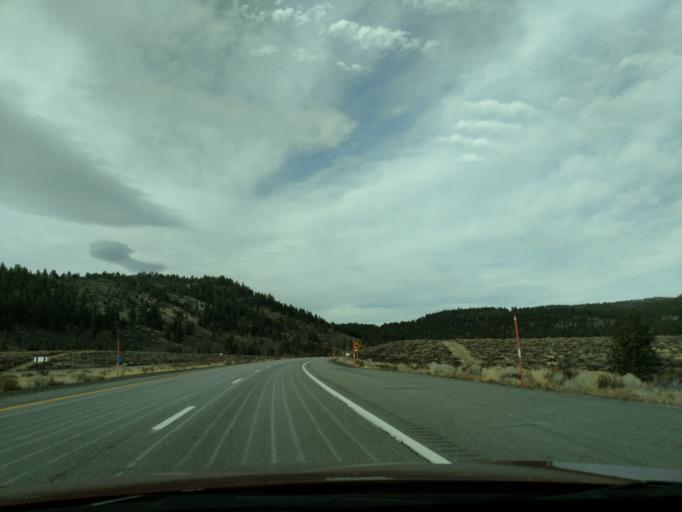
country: US
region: California
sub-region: Mono County
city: Mammoth Lakes
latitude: 37.6463
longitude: -118.9229
